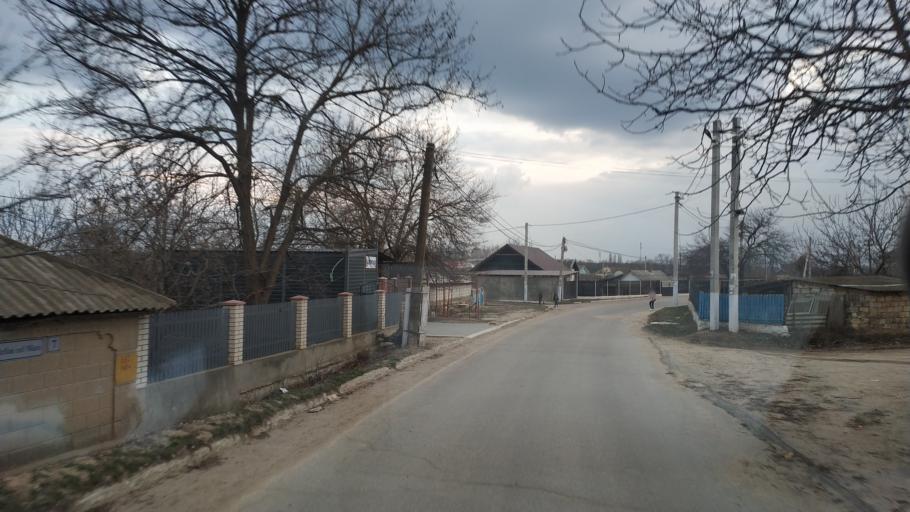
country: MD
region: Telenesti
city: Grigoriopol
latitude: 47.0232
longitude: 29.3587
